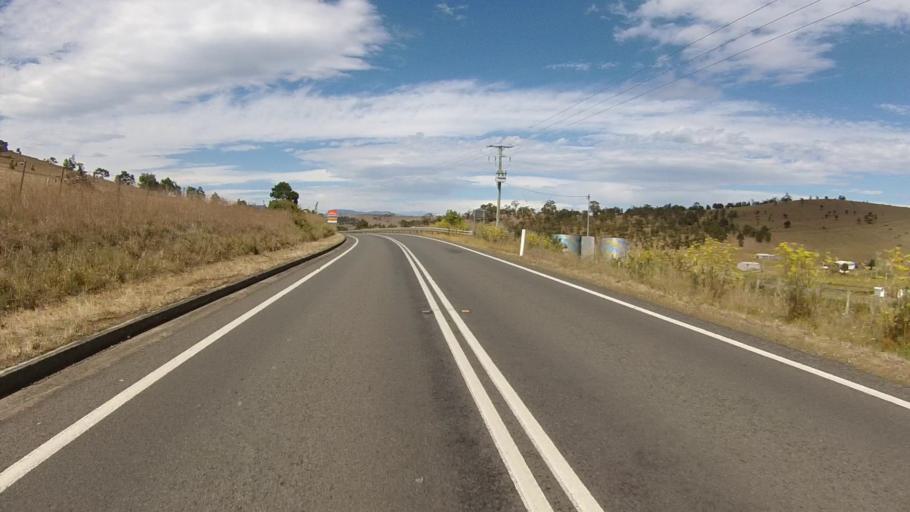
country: AU
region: Tasmania
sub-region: Brighton
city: Old Beach
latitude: -42.6791
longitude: 147.3546
